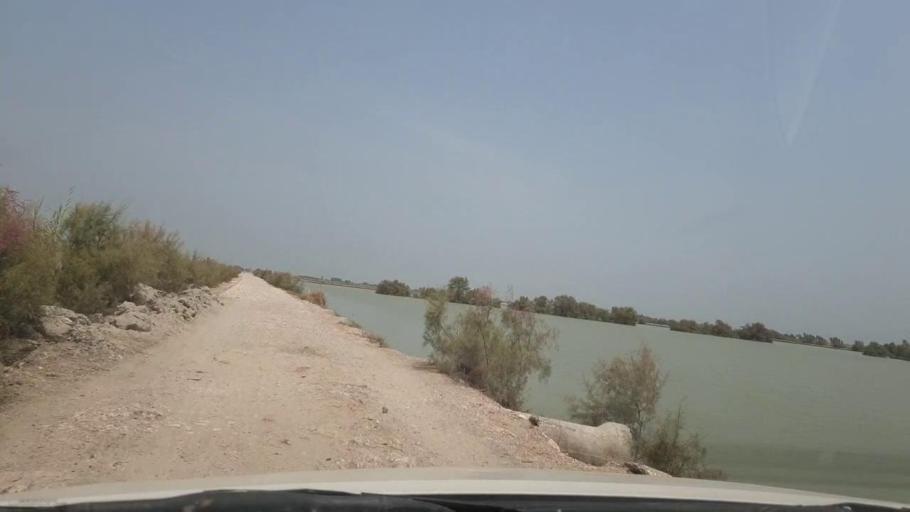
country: PK
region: Sindh
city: Rustam jo Goth
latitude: 28.0625
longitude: 68.8167
